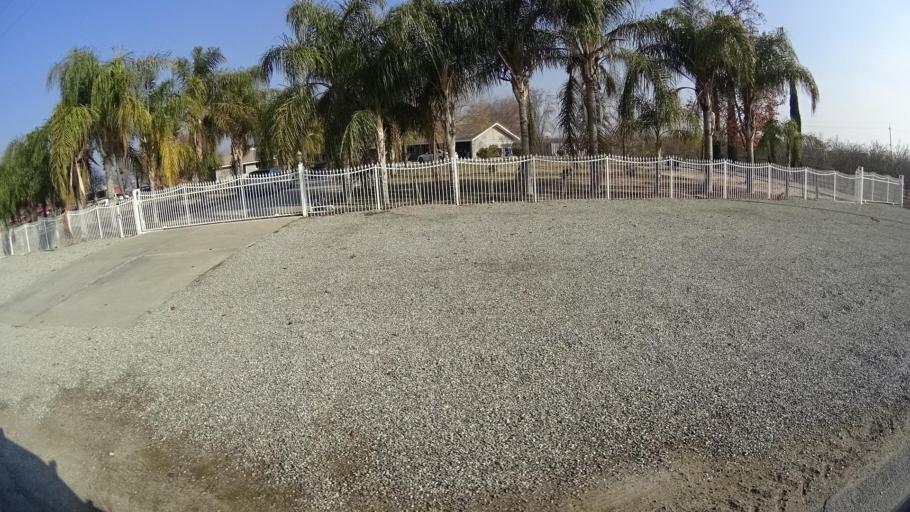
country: US
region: California
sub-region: Kern County
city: Greenfield
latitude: 35.2098
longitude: -119.0392
